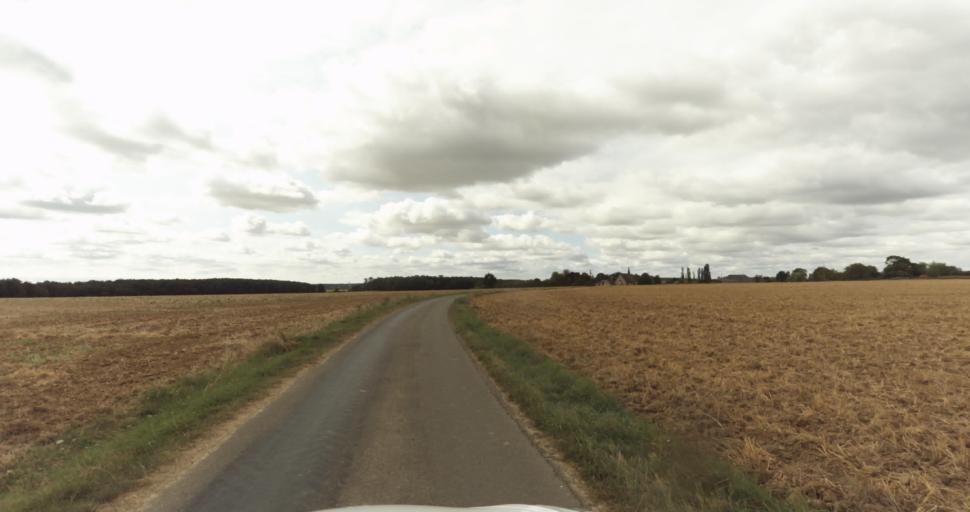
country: FR
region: Haute-Normandie
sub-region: Departement de l'Eure
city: Nonancourt
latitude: 48.7891
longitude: 1.1532
